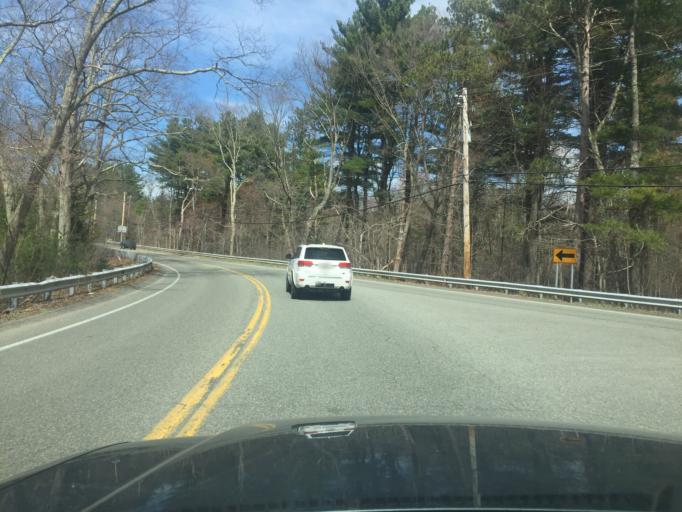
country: US
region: Massachusetts
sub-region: Norfolk County
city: Needham
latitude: 42.2585
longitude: -71.2373
